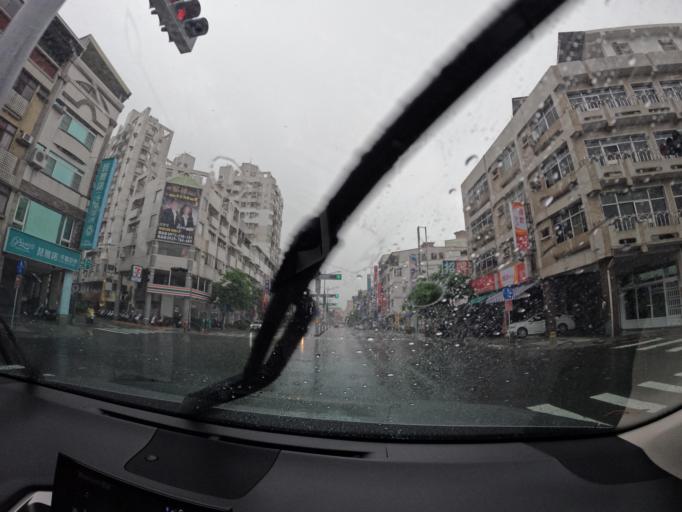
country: TW
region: Kaohsiung
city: Kaohsiung
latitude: 22.6688
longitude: 120.3136
